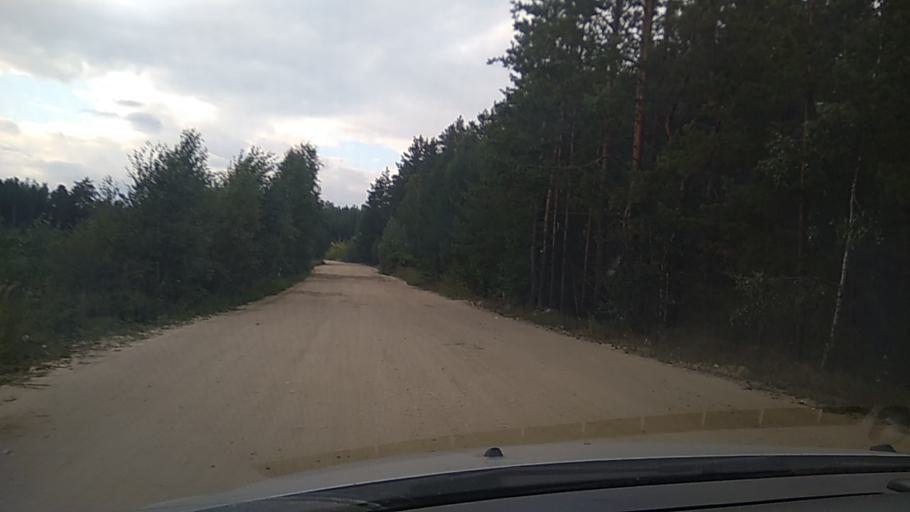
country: RU
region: Chelyabinsk
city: Kyshtym
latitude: 55.6820
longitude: 60.5726
